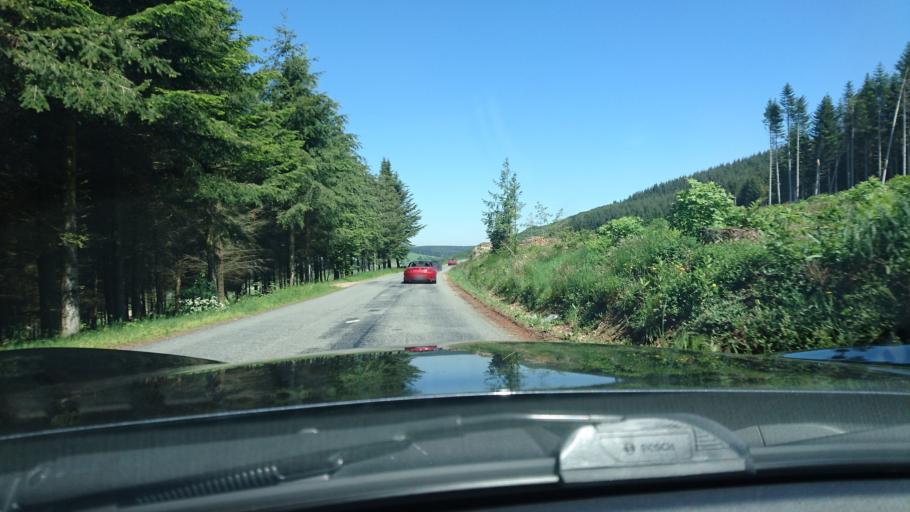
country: FR
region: Rhone-Alpes
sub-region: Departement de la Loire
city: Violay
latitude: 45.8742
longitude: 4.3377
